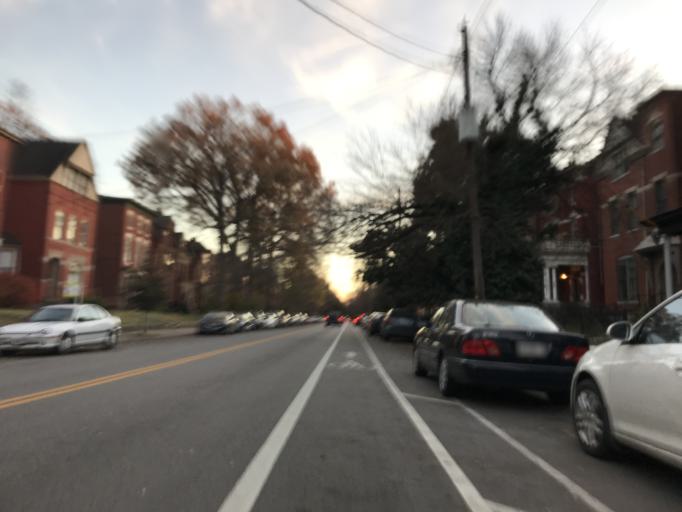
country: US
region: Kentucky
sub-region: Jefferson County
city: Louisville
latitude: 38.2339
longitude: -85.7555
